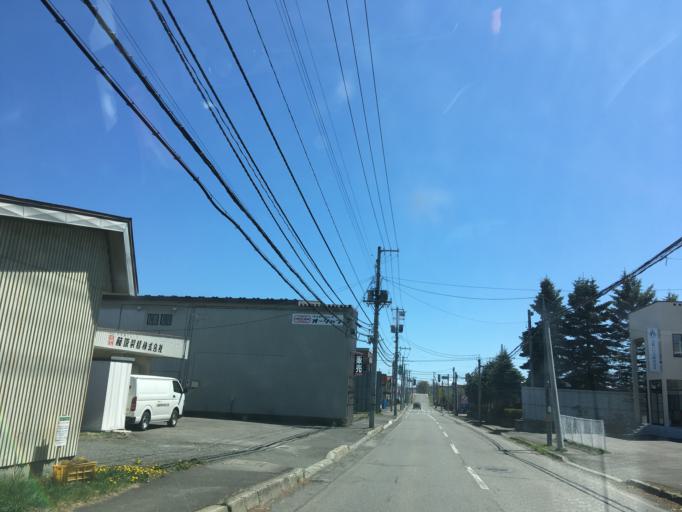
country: JP
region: Hokkaido
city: Obihiro
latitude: 42.9286
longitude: 143.1772
